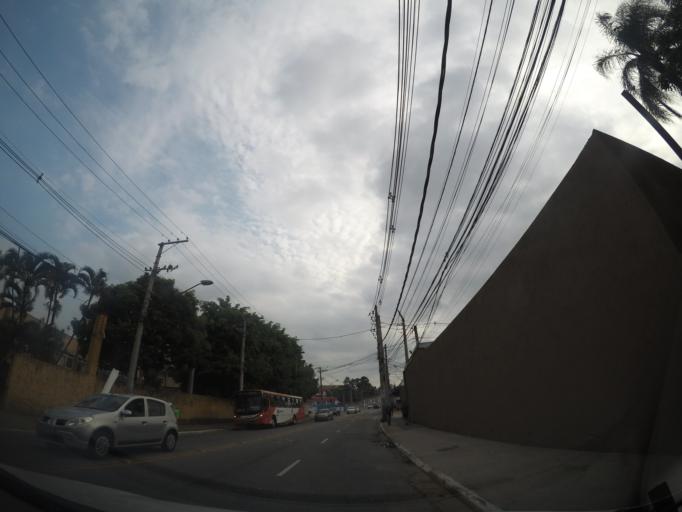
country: BR
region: Sao Paulo
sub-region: Guarulhos
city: Guarulhos
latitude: -23.4351
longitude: -46.5054
